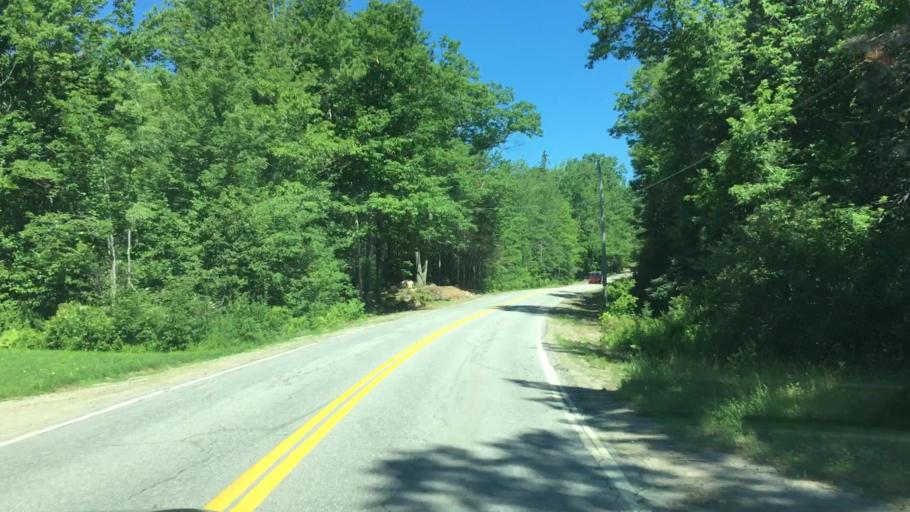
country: US
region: Maine
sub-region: Hancock County
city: Penobscot
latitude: 44.4280
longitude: -68.7129
